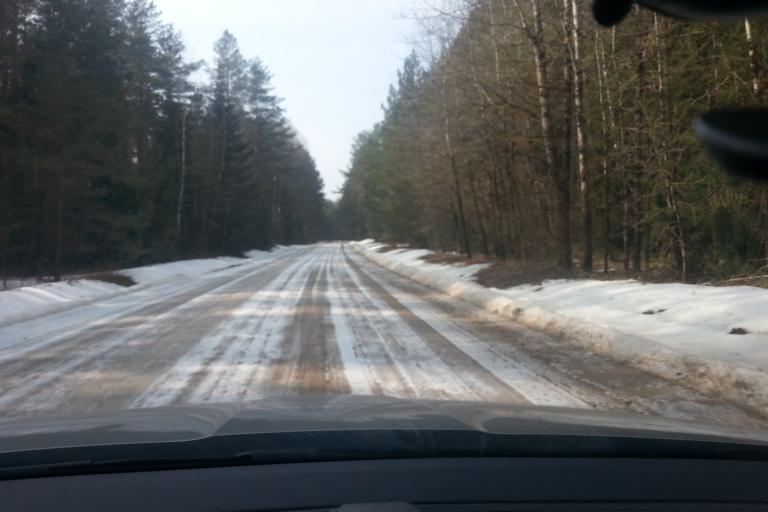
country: LT
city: Trakai
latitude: 54.5237
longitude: 24.9619
